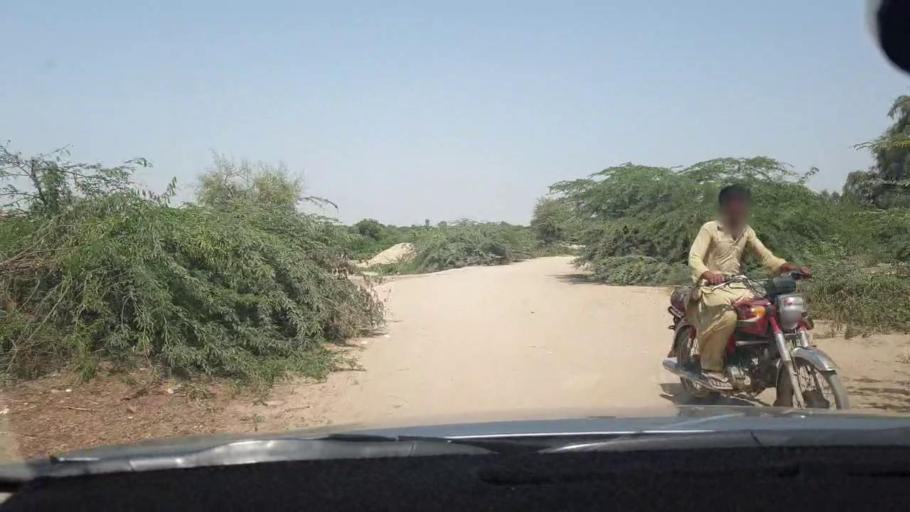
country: PK
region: Sindh
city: Tando Mittha Khan
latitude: 25.8544
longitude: 69.4246
